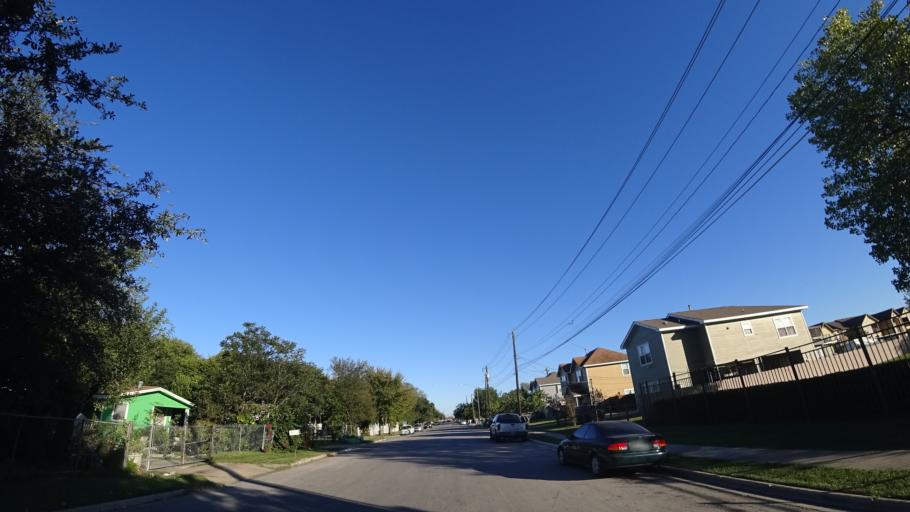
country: US
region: Texas
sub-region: Travis County
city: Austin
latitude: 30.2298
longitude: -97.7052
